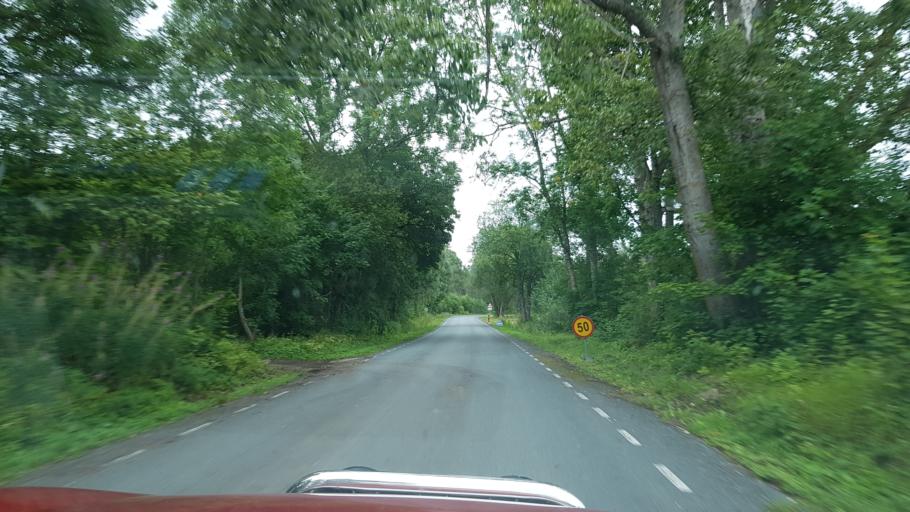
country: EE
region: Laeaene
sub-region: Lihula vald
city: Lihula
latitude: 58.8727
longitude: 23.9133
